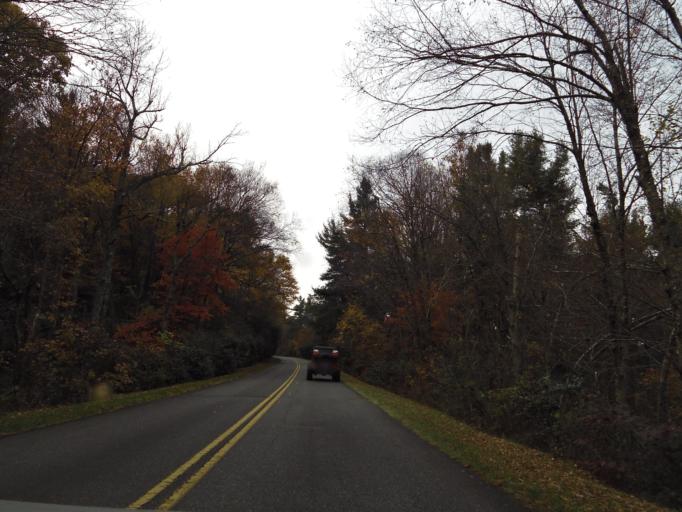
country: US
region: North Carolina
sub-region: Ashe County
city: West Jefferson
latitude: 36.2449
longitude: -81.4669
